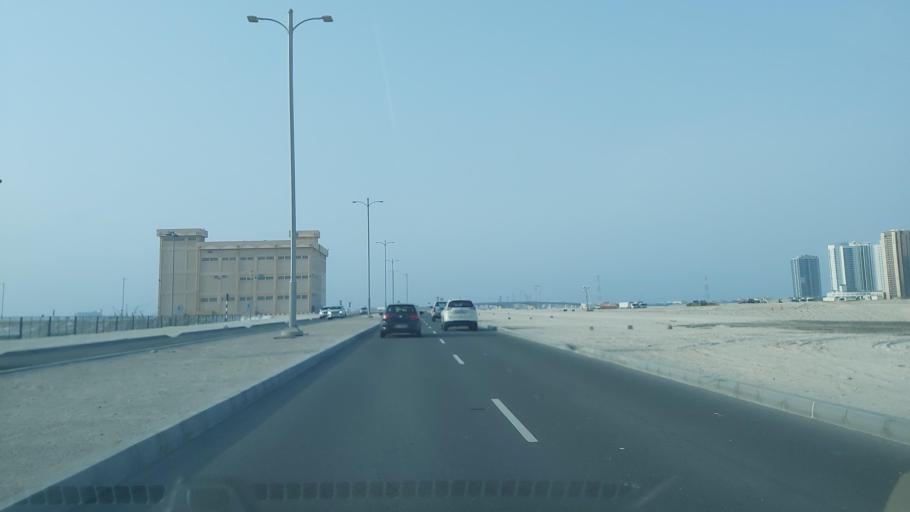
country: AE
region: Abu Dhabi
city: Abu Dhabi
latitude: 24.5002
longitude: 54.3958
